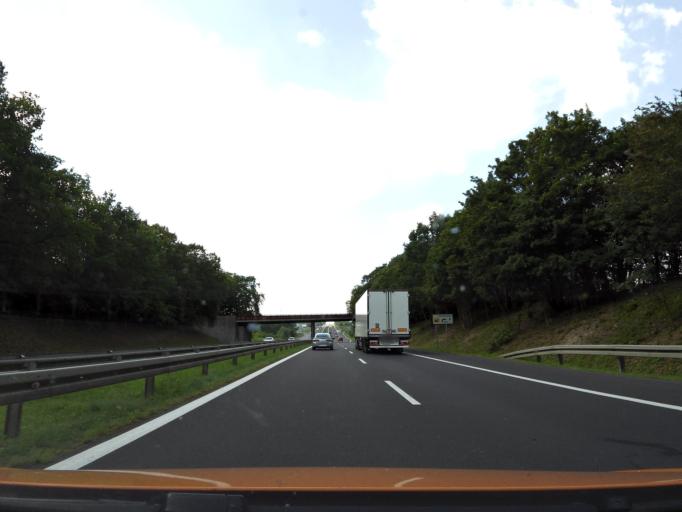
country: PL
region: West Pomeranian Voivodeship
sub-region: Powiat policki
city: Kolbaskowo
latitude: 53.3392
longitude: 14.4333
